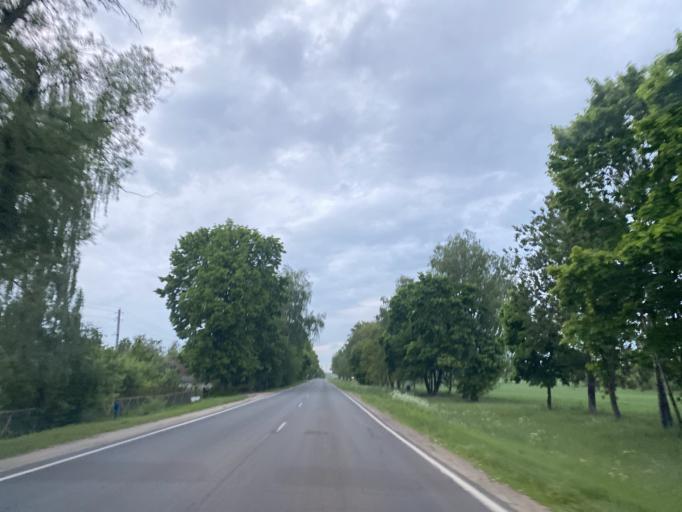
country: BY
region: Minsk
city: Rudzyensk
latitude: 53.6129
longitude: 27.8565
